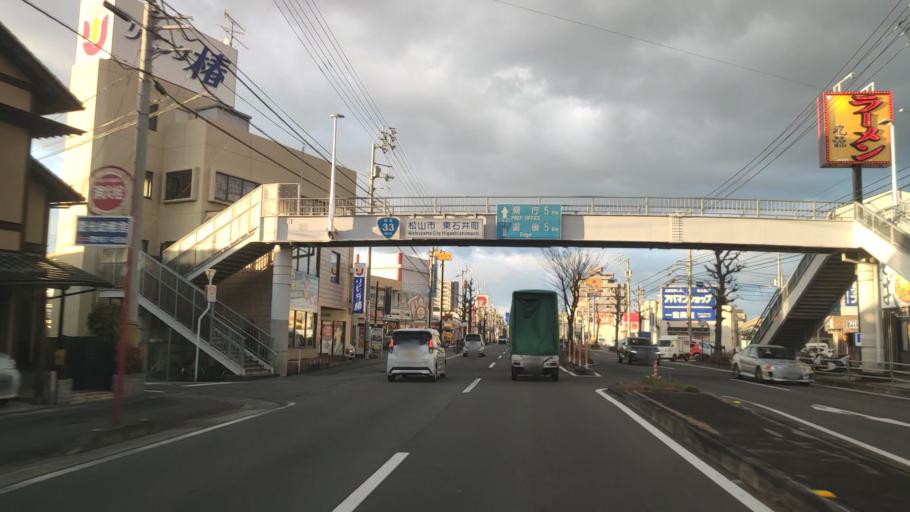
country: JP
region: Ehime
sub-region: Shikoku-chuo Shi
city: Matsuyama
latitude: 33.8101
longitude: 132.7797
